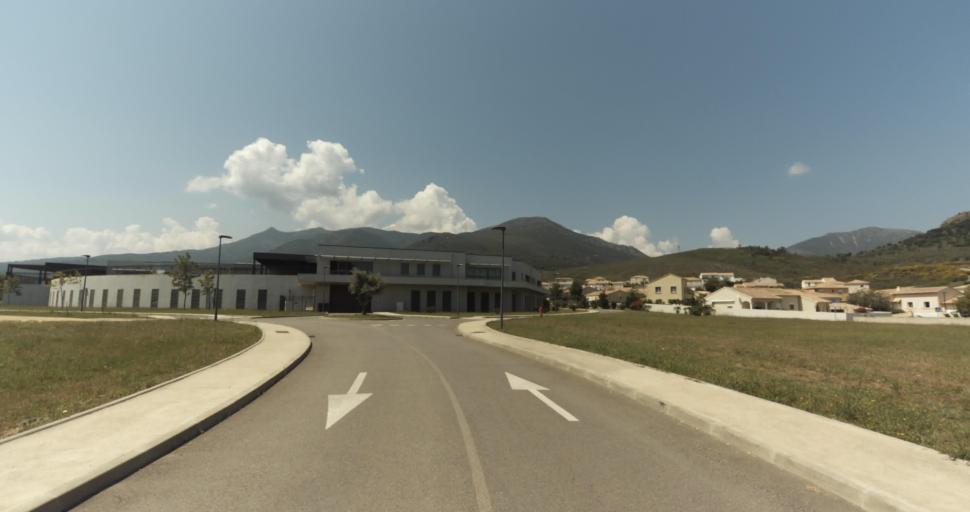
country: FR
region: Corsica
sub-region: Departement de la Haute-Corse
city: Biguglia
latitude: 42.6009
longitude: 9.4346
